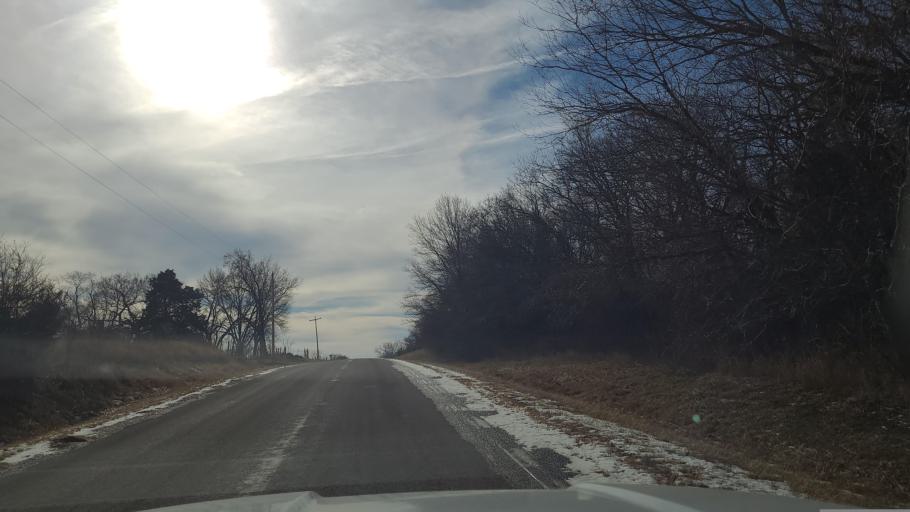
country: US
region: Kansas
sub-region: Douglas County
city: Lawrence
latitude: 38.8957
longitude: -95.1863
